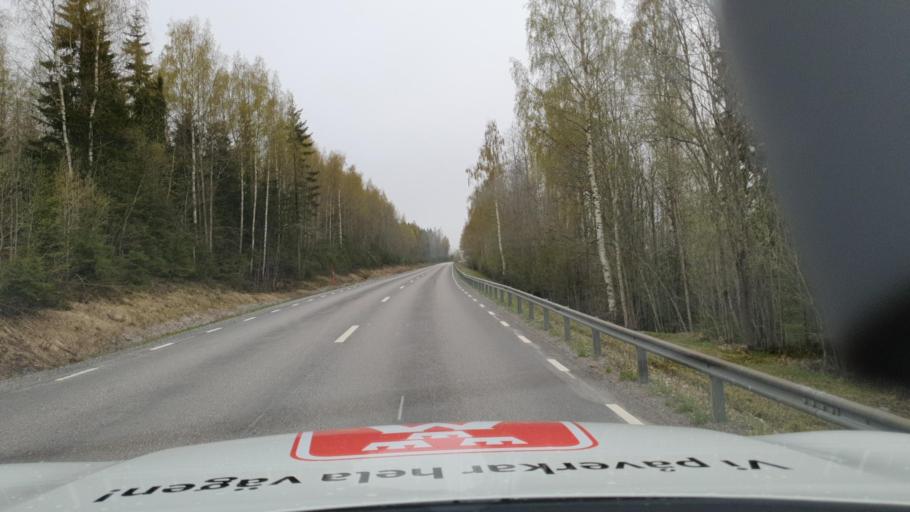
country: SE
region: Vaesterbotten
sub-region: Vannas Kommun
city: Vaennaes
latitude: 63.7861
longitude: 19.8333
